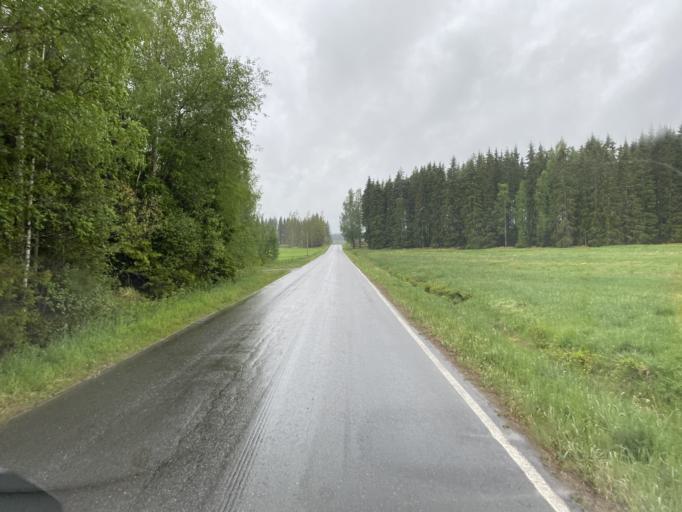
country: FI
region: Haeme
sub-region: Forssa
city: Humppila
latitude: 61.0602
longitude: 23.3249
